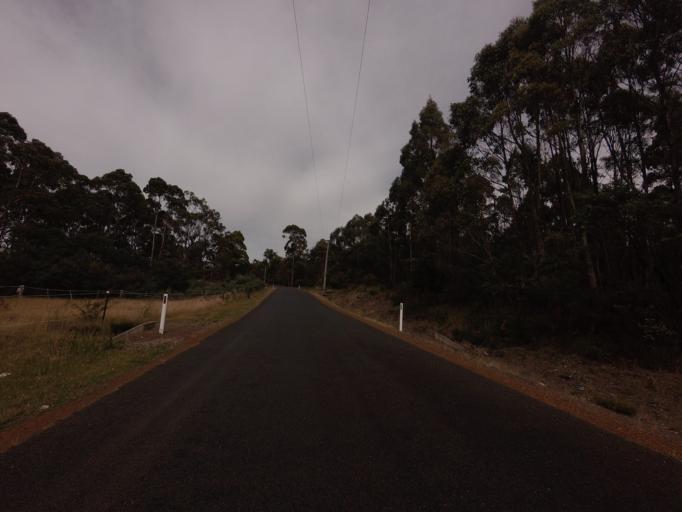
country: AU
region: Tasmania
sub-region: Sorell
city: Sorell
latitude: -42.5555
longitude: 147.5669
